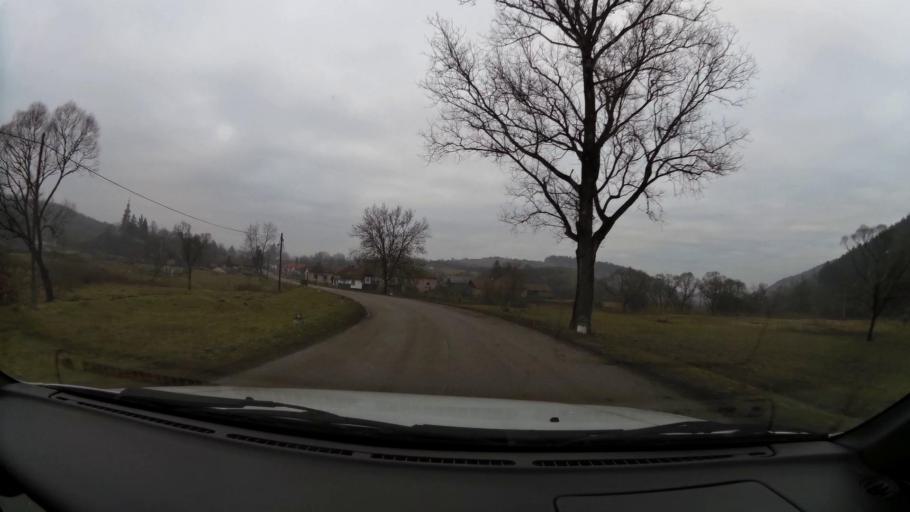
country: HU
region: Borsod-Abauj-Zemplen
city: Rudabanya
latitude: 48.4073
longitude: 20.6583
